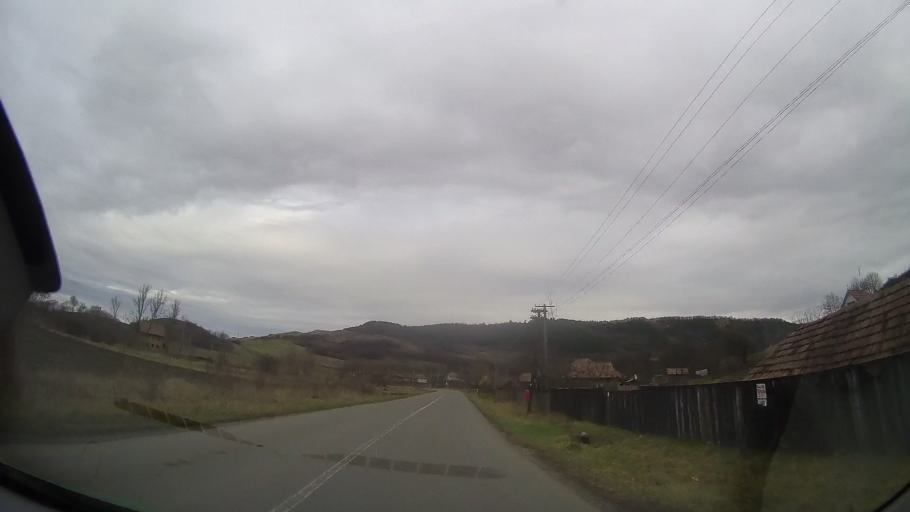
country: RO
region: Mures
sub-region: Comuna Faragau
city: Faragau
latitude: 46.7333
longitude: 24.5445
